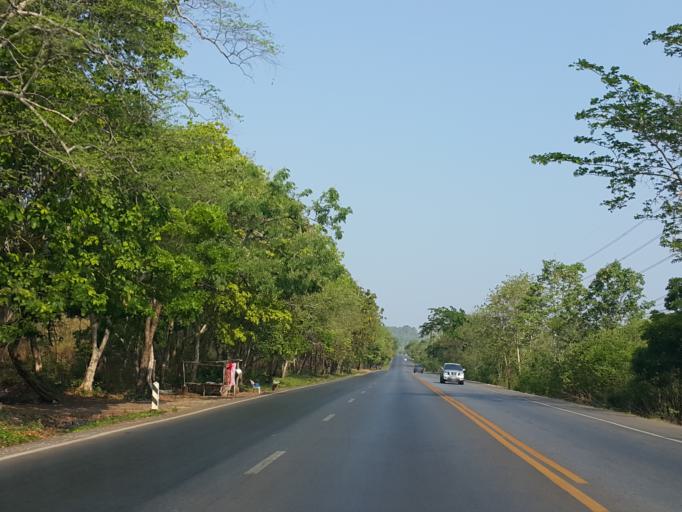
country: TH
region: Kanchanaburi
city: Sai Yok
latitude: 14.1073
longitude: 99.2169
